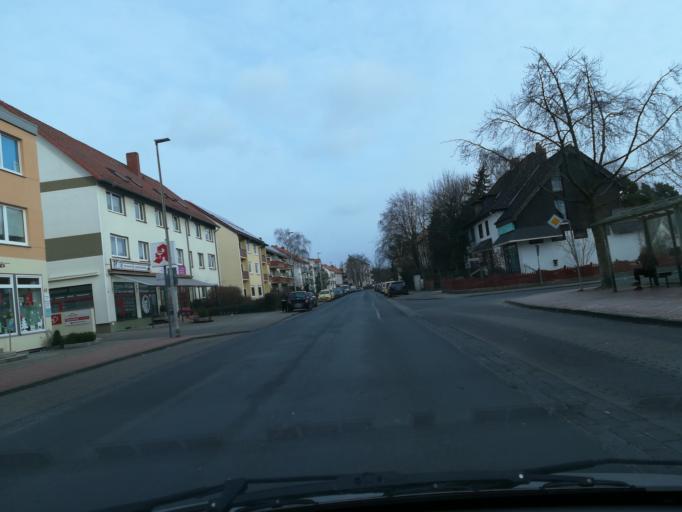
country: DE
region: Lower Saxony
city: Seelze
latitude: 52.3945
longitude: 9.5995
